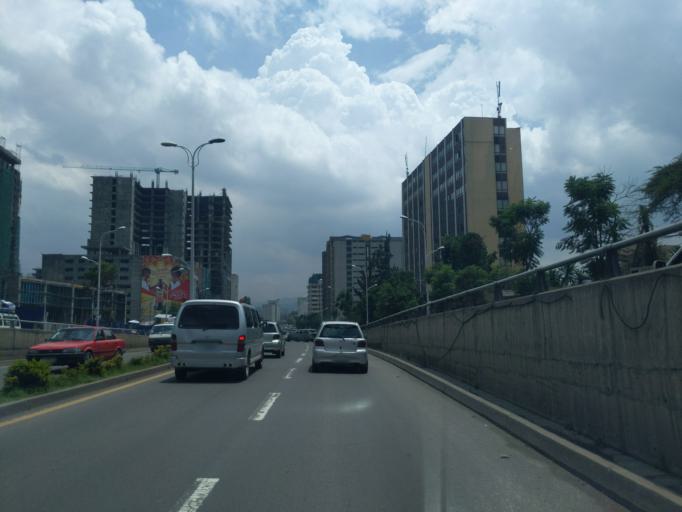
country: ET
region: Adis Abeba
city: Addis Ababa
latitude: 9.0062
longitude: 38.7671
